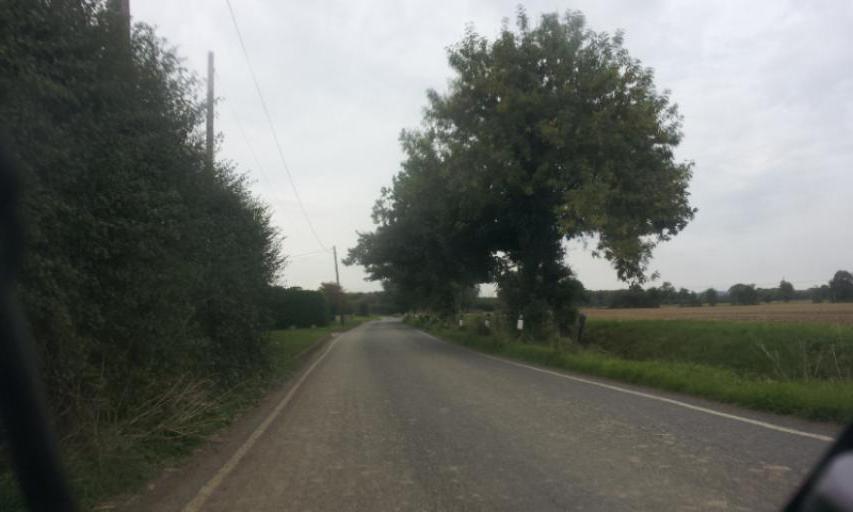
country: GB
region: England
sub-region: Kent
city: Hadlow
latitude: 51.1934
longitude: 0.3206
